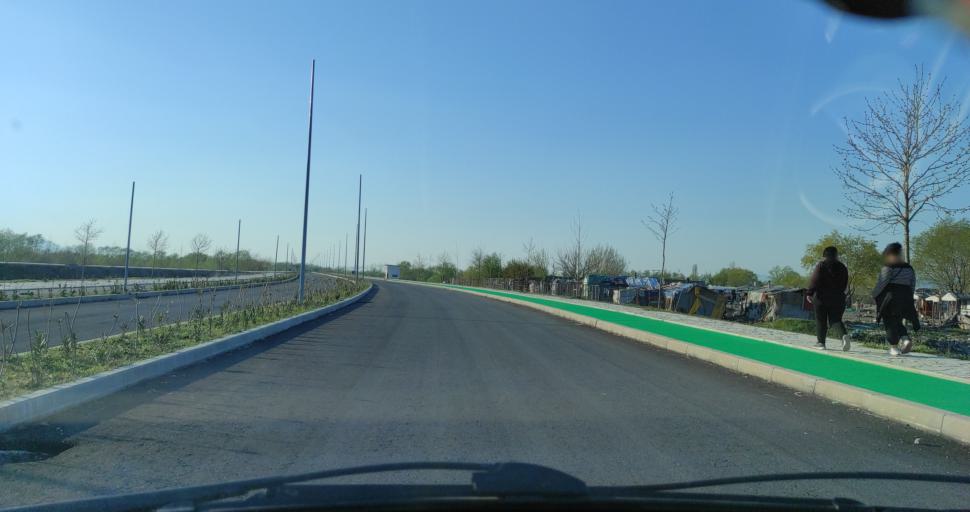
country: AL
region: Shkoder
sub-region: Rrethi i Shkodres
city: Shkoder
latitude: 42.0594
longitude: 19.4975
